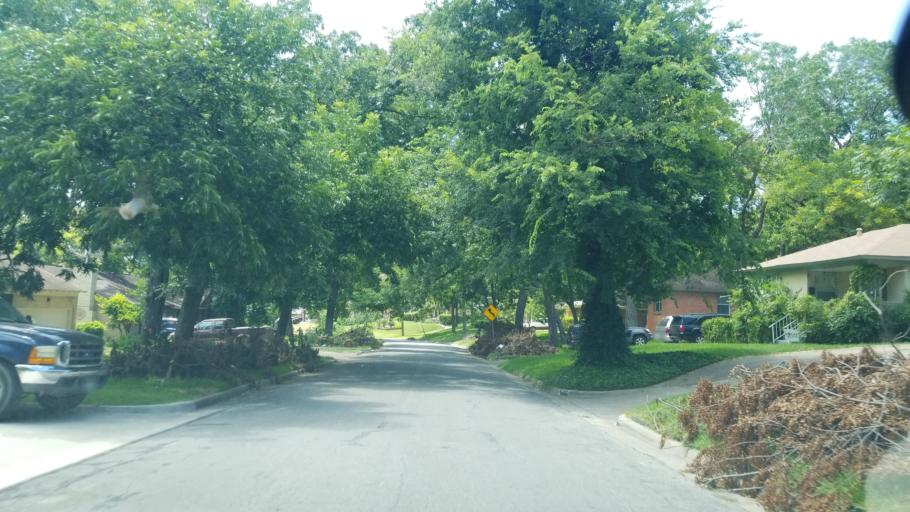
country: US
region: Texas
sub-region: Dallas County
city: Balch Springs
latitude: 32.7571
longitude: -96.6965
